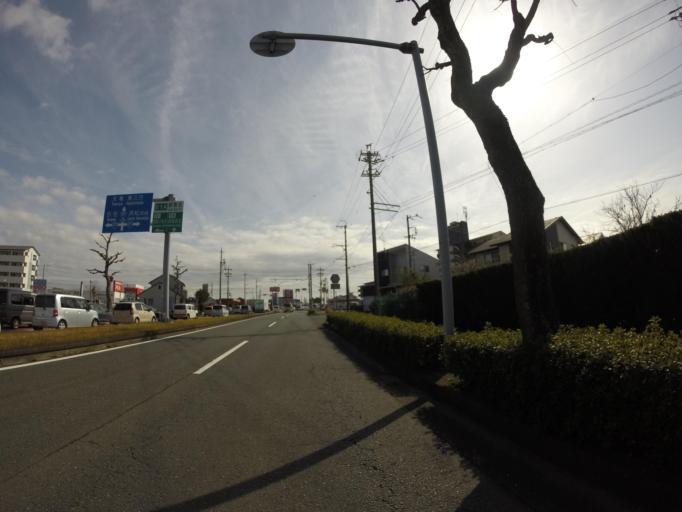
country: JP
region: Shizuoka
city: Hamakita
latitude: 34.7796
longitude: 137.7092
